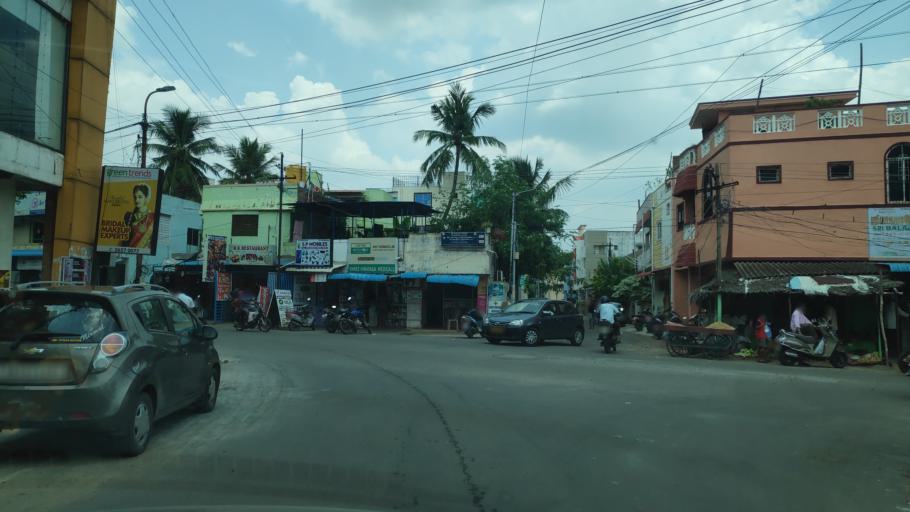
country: IN
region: Tamil Nadu
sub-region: Thiruvallur
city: Ambattur
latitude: 13.1176
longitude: 80.1565
